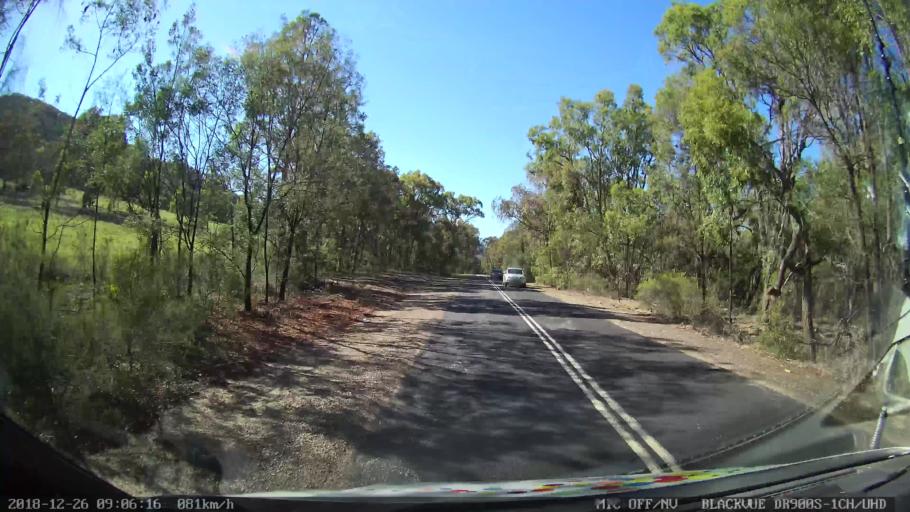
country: AU
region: New South Wales
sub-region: Mid-Western Regional
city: Kandos
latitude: -32.6921
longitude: 150.0048
